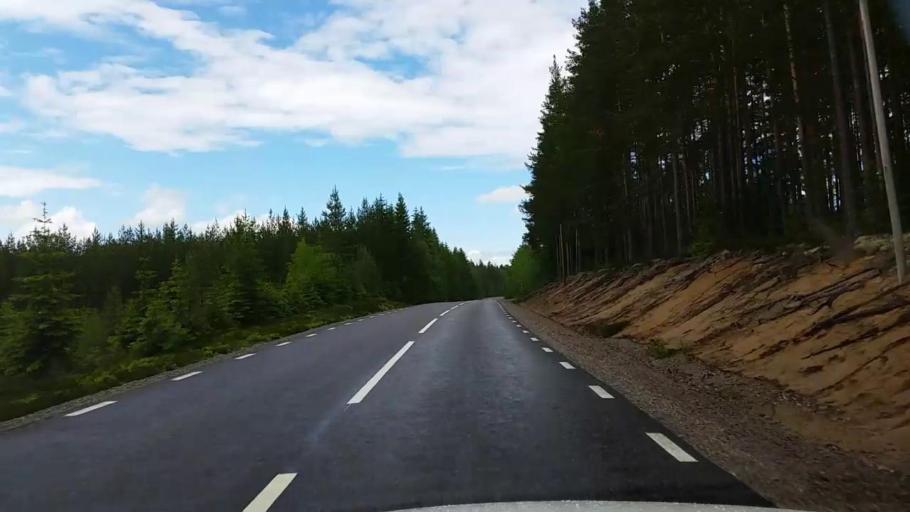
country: SE
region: Gaevleborg
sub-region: Sandvikens Kommun
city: Jarbo
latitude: 60.8499
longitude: 16.4519
